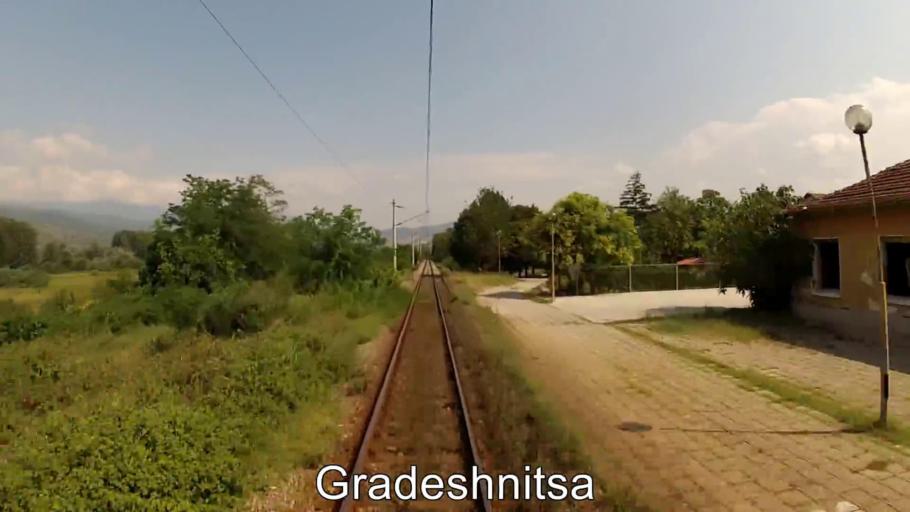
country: BG
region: Blagoevgrad
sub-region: Obshtina Strumyani
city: Strumyani
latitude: 41.6571
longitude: 23.1780
